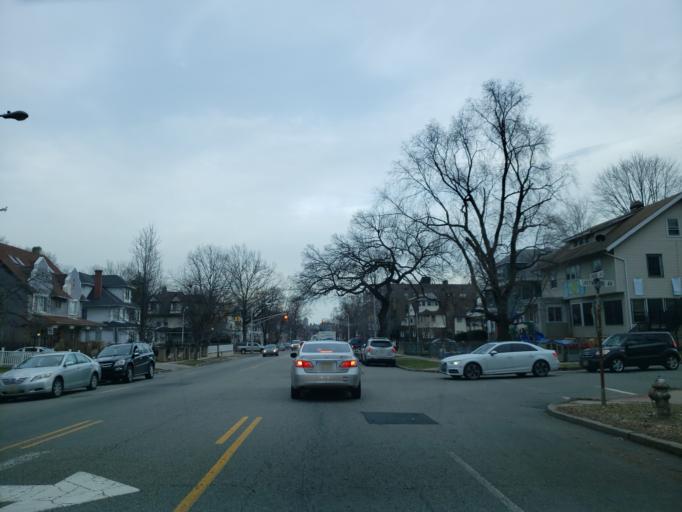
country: US
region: New Jersey
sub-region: Essex County
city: East Orange
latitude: 40.7638
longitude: -74.1991
